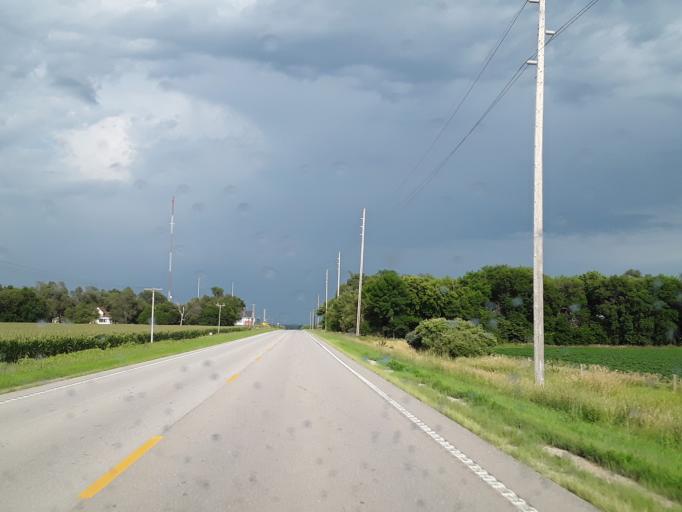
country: US
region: Nebraska
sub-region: Saunders County
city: Ashland
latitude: 41.0886
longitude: -96.3917
